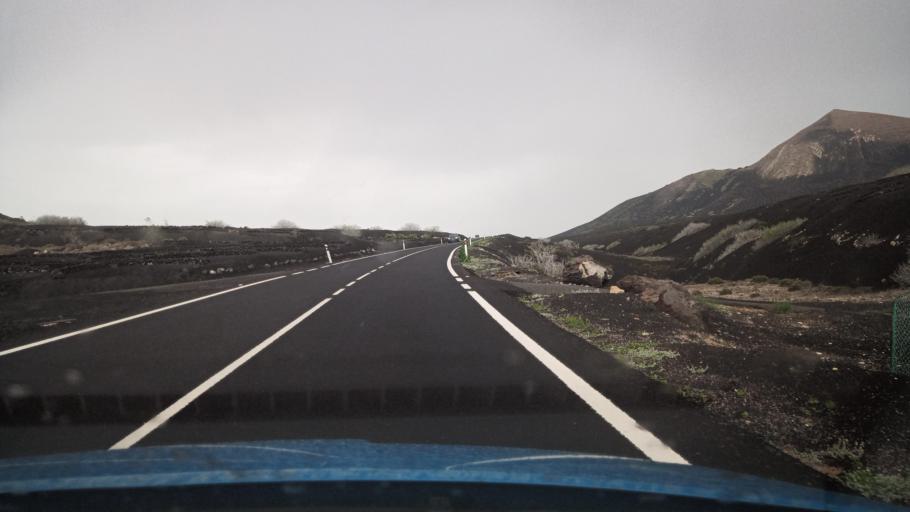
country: ES
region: Canary Islands
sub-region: Provincia de Las Palmas
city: Yaiza
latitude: 28.9633
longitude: -13.7257
